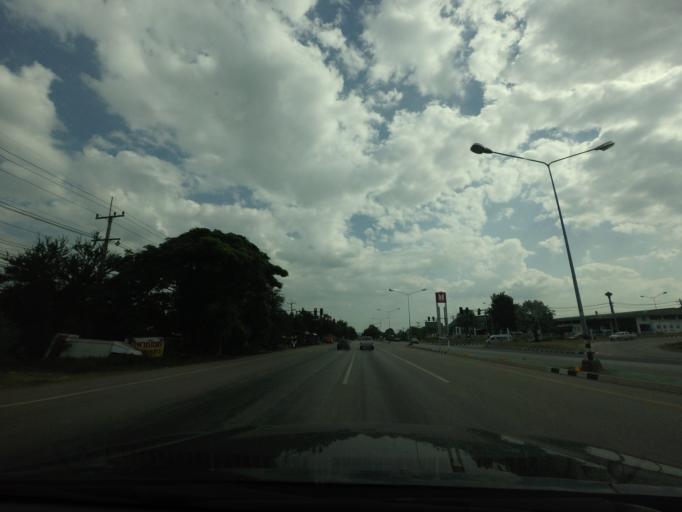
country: TH
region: Lop Buri
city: Chai Badan
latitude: 15.2340
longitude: 101.1267
